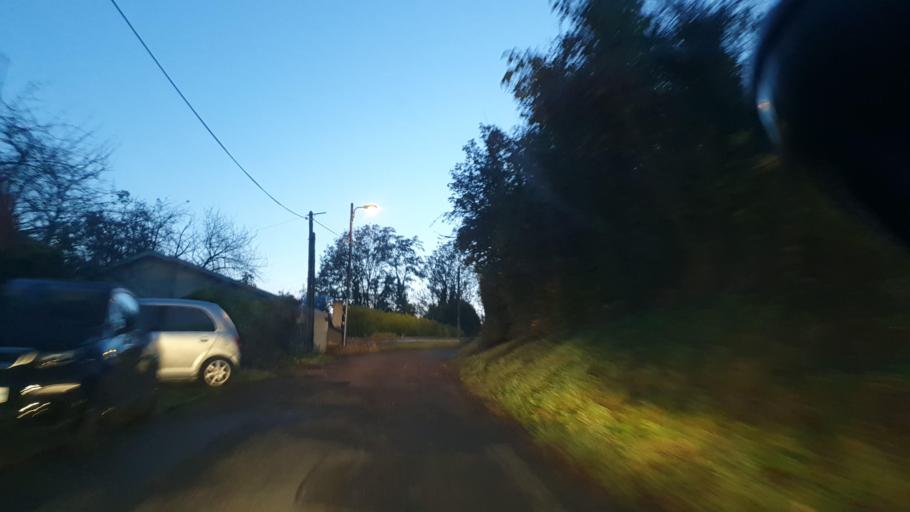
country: FR
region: Rhone-Alpes
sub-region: Departement du Rhone
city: Albigny-sur-Saone
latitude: 45.8416
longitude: 4.8210
